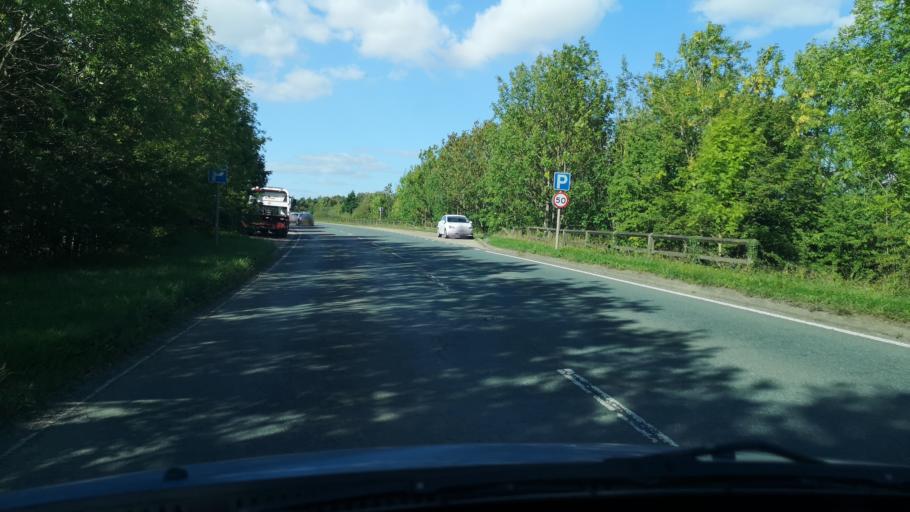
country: GB
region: England
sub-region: North Lincolnshire
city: Belton
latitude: 53.5646
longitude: -0.8181
